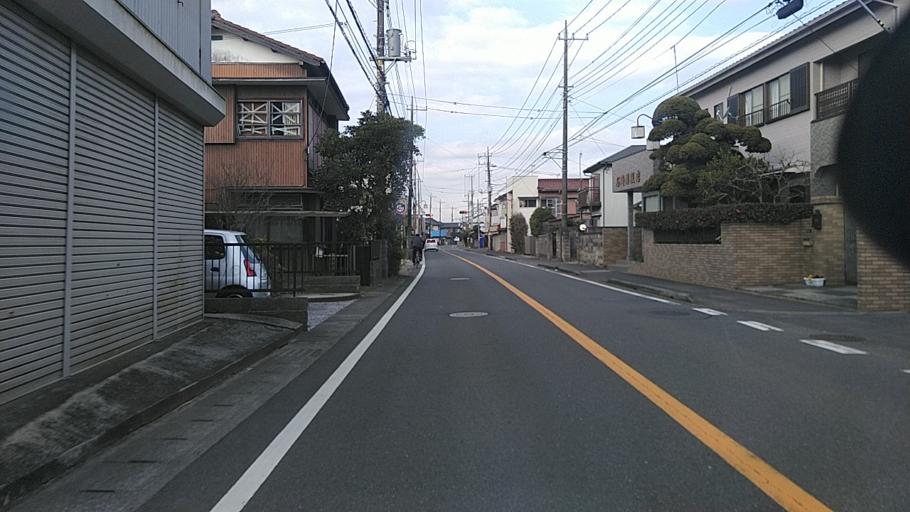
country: JP
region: Chiba
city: Togane
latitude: 35.5579
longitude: 140.3540
